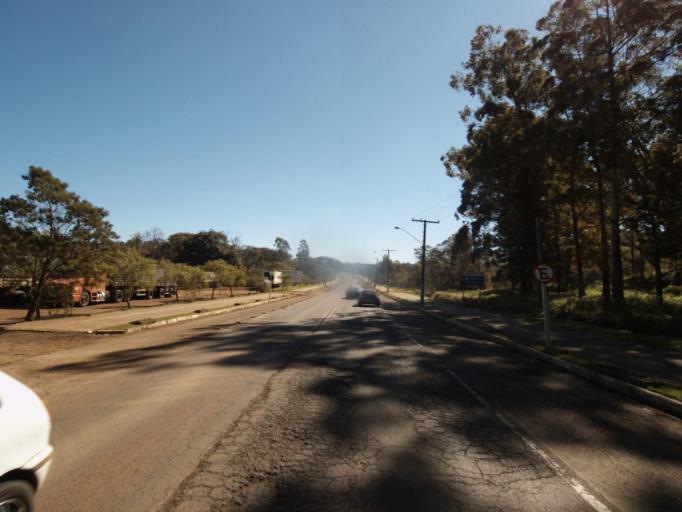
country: AR
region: Misiones
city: Bernardo de Irigoyen
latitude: -26.7550
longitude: -53.5072
